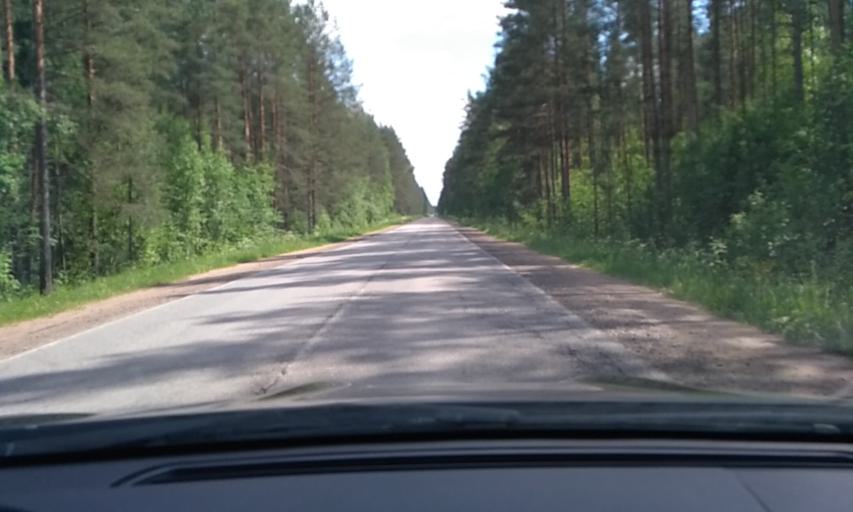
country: RU
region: Leningrad
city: Imeni Sverdlova
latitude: 59.8406
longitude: 30.6933
